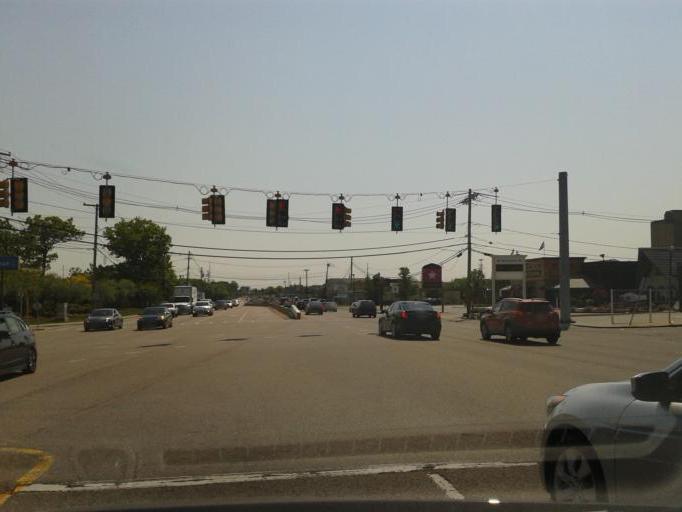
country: US
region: Massachusetts
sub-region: Middlesex County
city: Framingham
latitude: 42.2987
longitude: -71.4002
